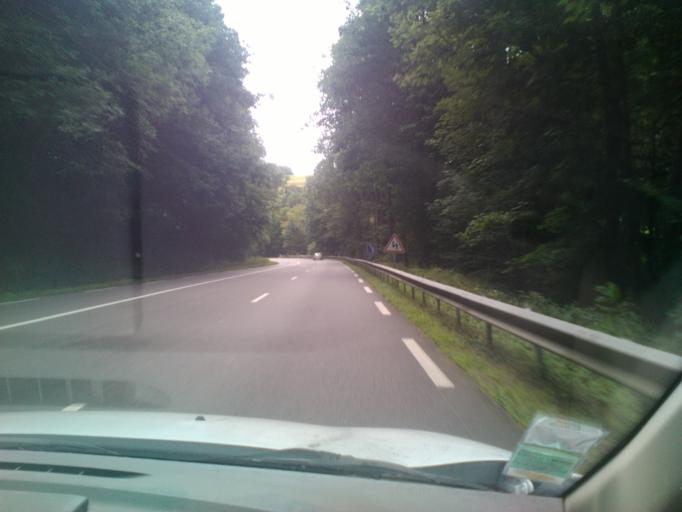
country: FR
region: Alsace
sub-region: Departement du Haut-Rhin
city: Lapoutroie
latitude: 48.1649
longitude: 7.1509
